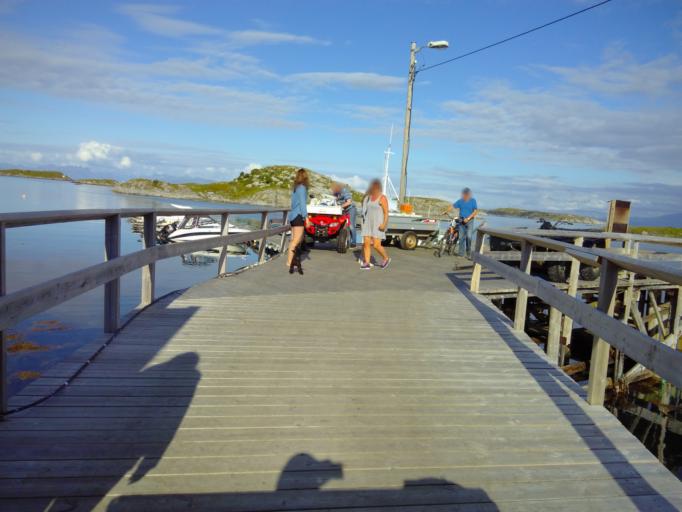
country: NO
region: Nordland
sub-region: Gildeskal
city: Inndyr
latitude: 67.2769
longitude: 14.0063
